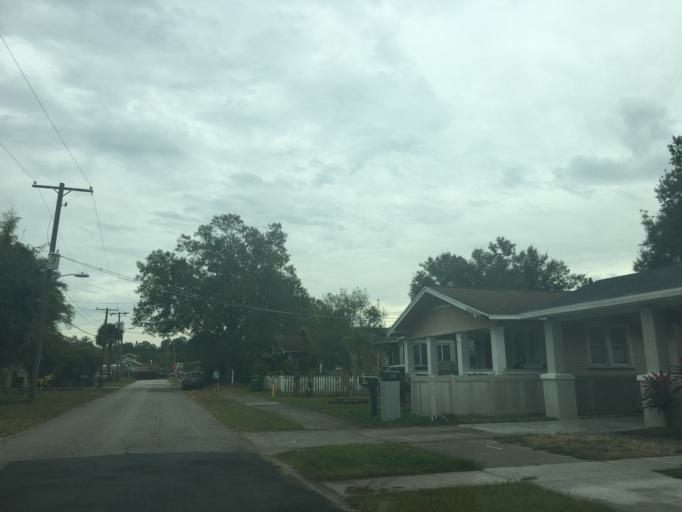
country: US
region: Florida
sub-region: Hillsborough County
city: Tampa
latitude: 27.9852
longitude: -82.4608
